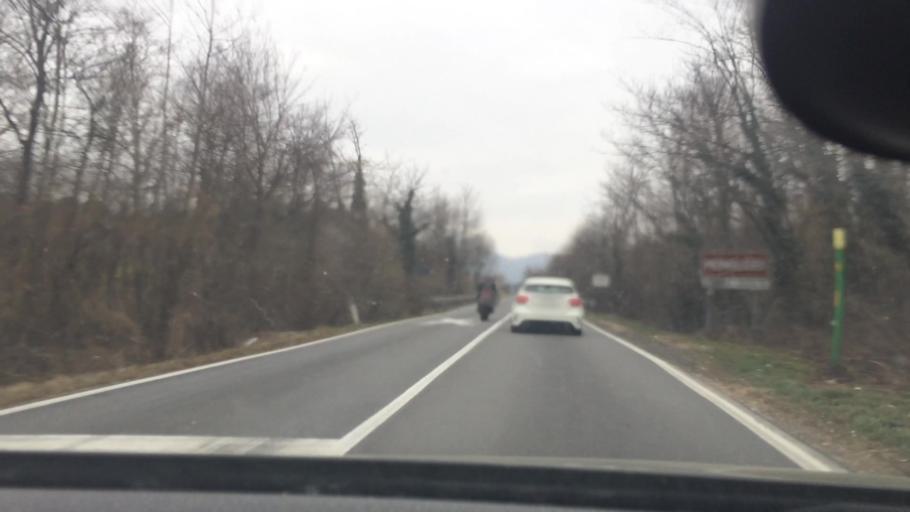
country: IT
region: Lombardy
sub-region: Provincia di Como
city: Nobile-Monguzzo
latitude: 45.7688
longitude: 9.2296
